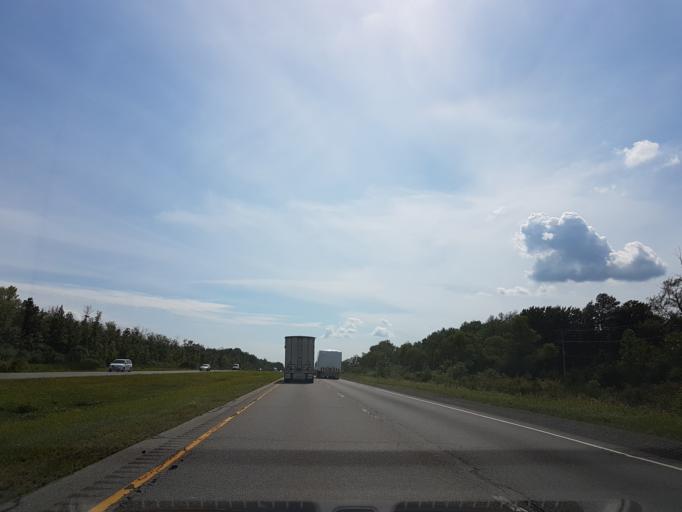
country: CA
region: Ontario
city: Prescott
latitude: 44.6928
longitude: -75.5788
